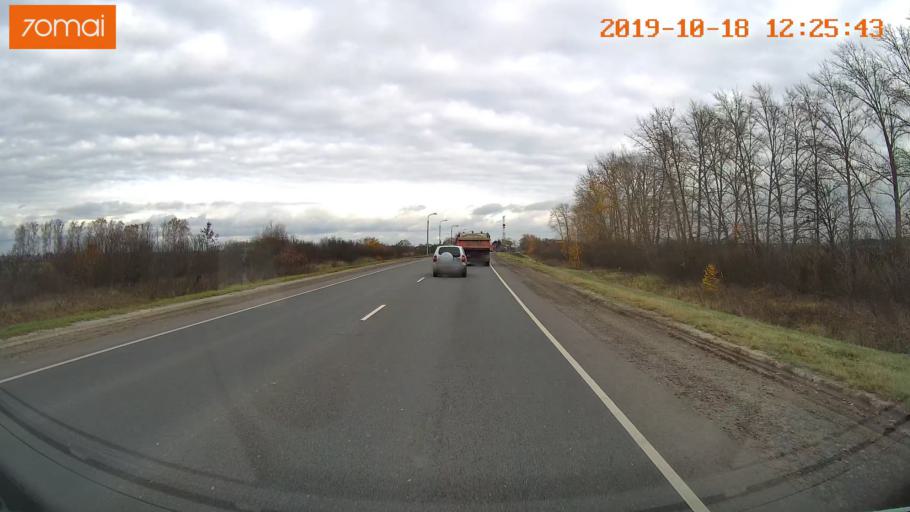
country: RU
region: Rjazan
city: Rybnoye
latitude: 54.5525
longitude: 39.5235
